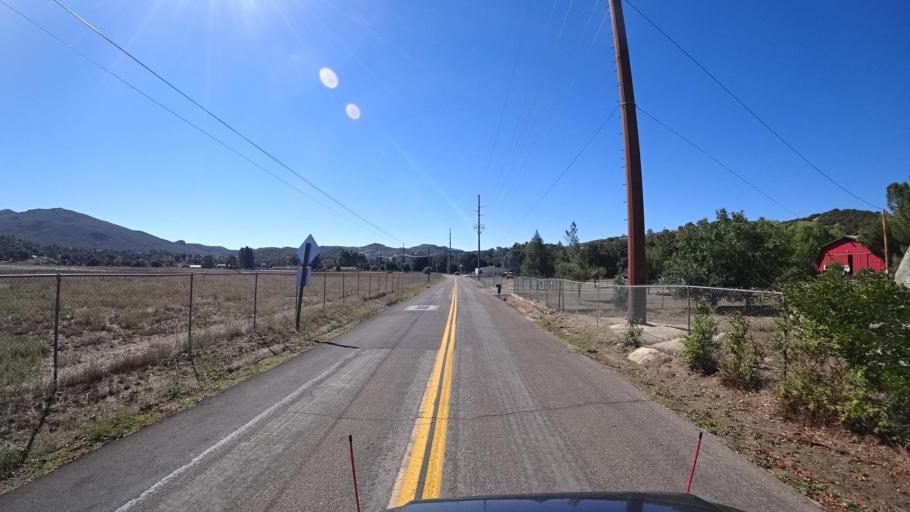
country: US
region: California
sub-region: San Diego County
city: Descanso
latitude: 32.8634
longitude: -116.6162
